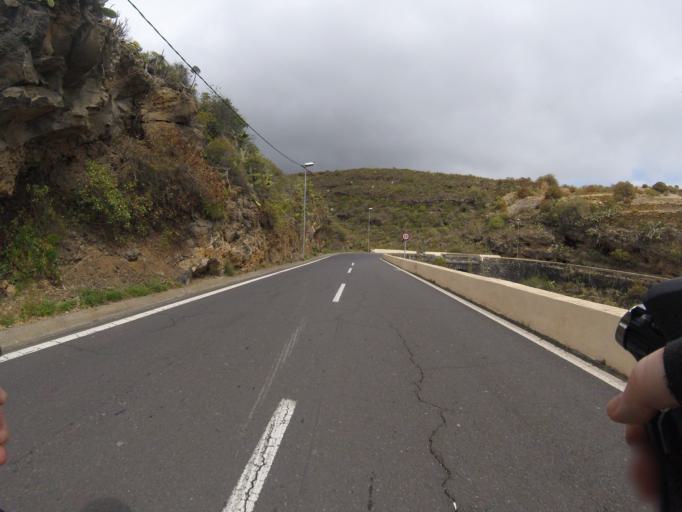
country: ES
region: Canary Islands
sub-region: Provincia de Santa Cruz de Tenerife
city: Guimar
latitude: 28.2752
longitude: -16.4139
